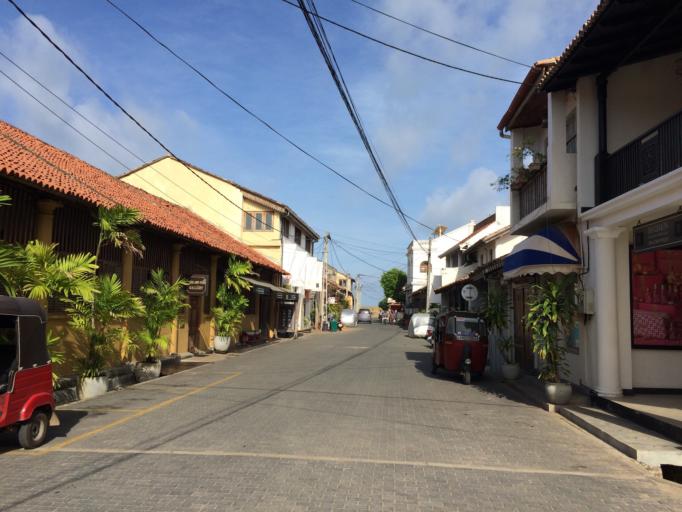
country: LK
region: Southern
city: Galle
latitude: 6.0262
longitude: 80.2168
